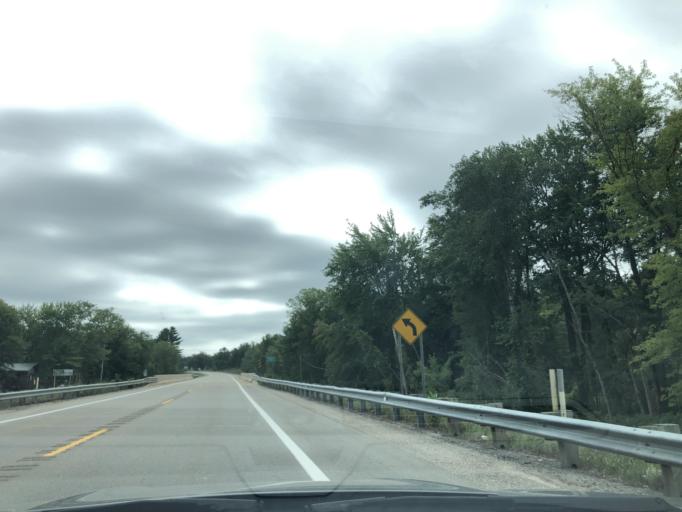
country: US
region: Michigan
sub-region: Clare County
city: Harrison
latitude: 44.0381
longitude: -85.0348
